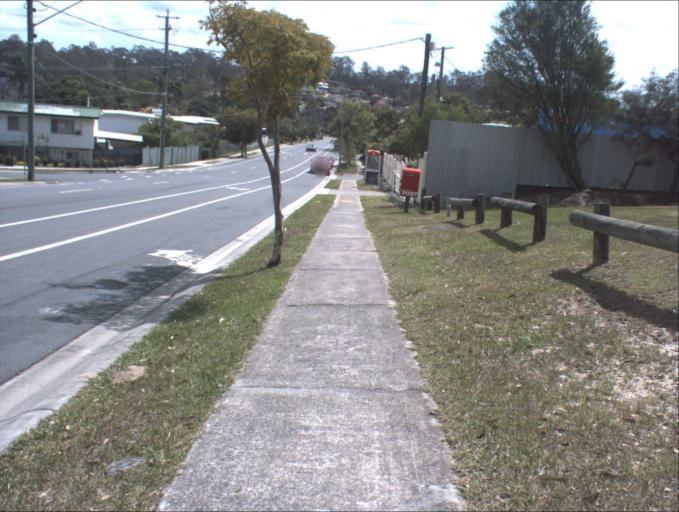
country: AU
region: Queensland
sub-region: Logan
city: Woodridge
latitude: -27.6216
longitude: 153.0995
